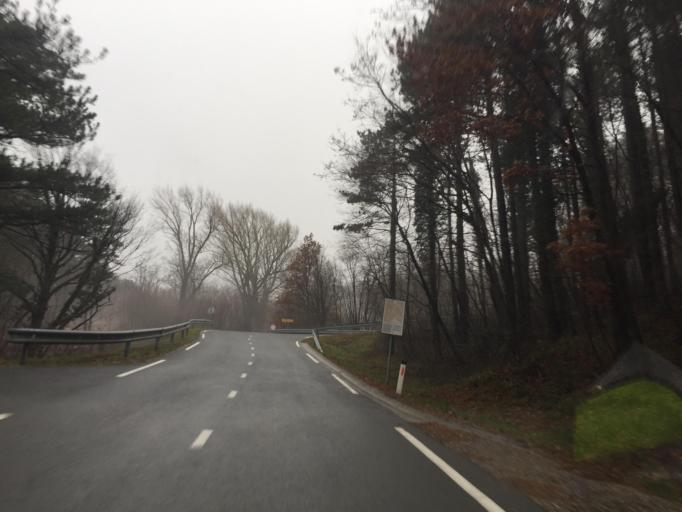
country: SI
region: Ajdovscina
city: Lokavec
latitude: 45.9169
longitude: 13.8918
